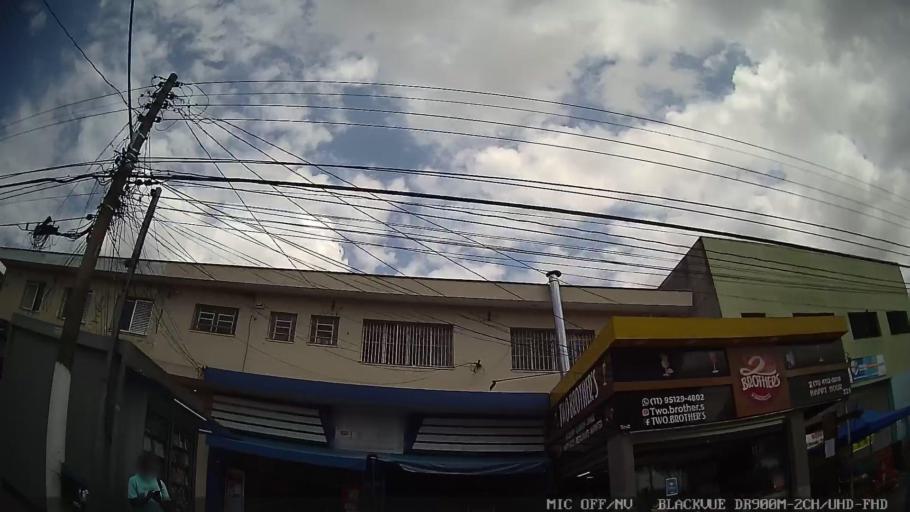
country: BR
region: Sao Paulo
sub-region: Guarulhos
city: Guarulhos
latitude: -23.5145
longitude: -46.4966
